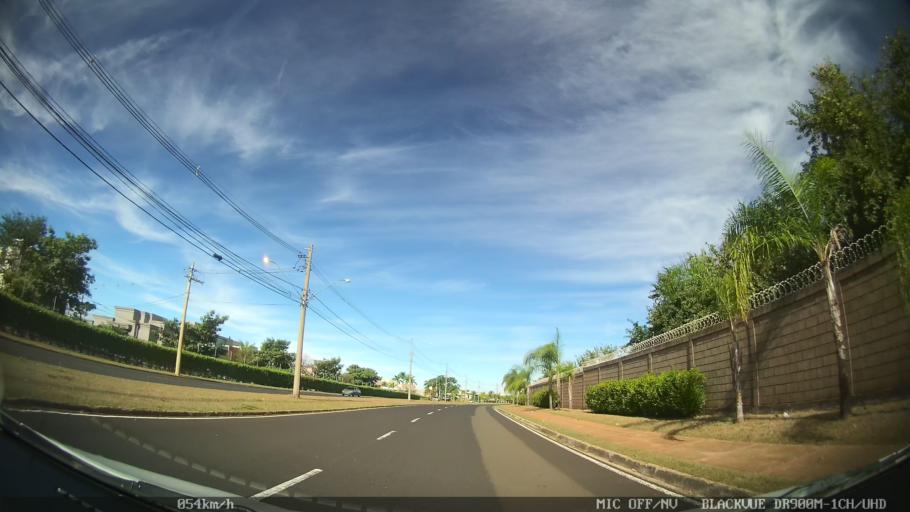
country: BR
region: Sao Paulo
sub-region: Sao Jose Do Rio Preto
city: Sao Jose do Rio Preto
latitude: -20.8081
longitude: -49.3306
